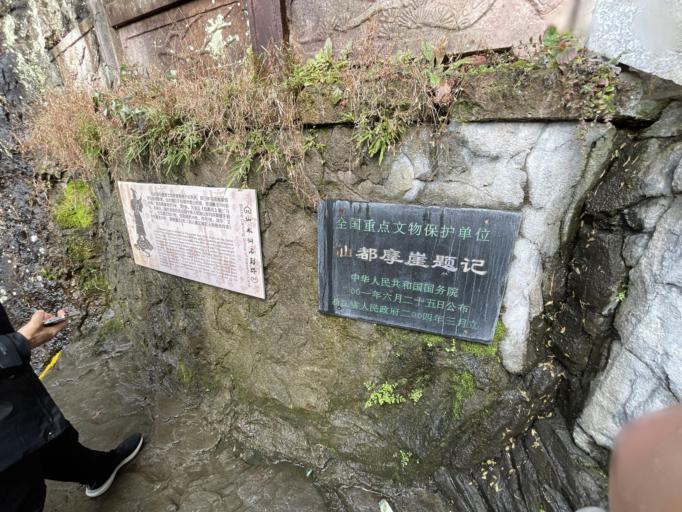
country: CN
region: Zhejiang Sheng
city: Shuhong
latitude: 28.6933
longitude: 120.1396
